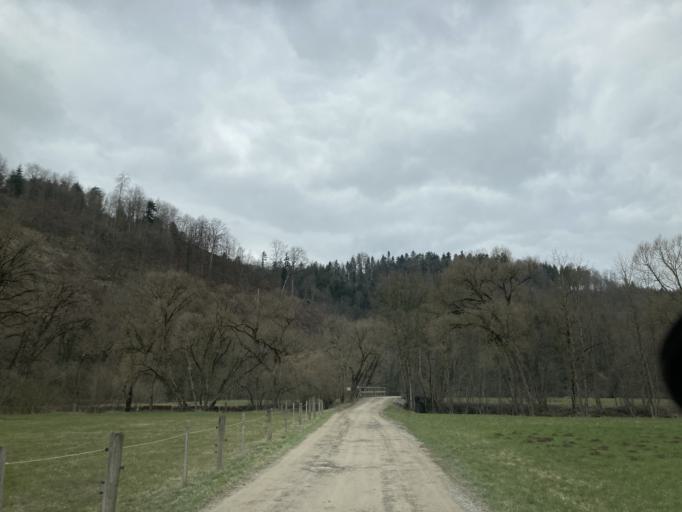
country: DE
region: Baden-Wuerttemberg
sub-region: Tuebingen Region
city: Hirrlingen
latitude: 48.4182
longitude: 8.8670
